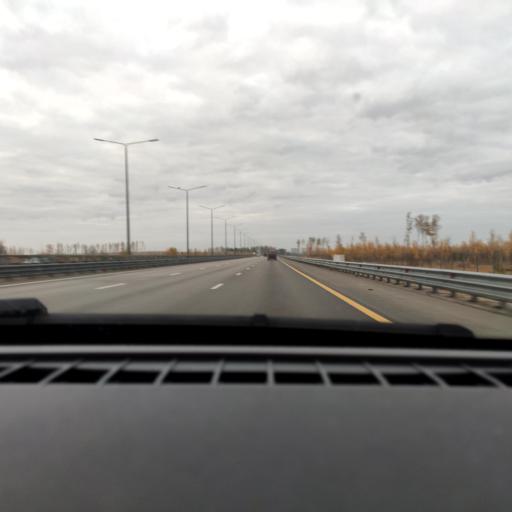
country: RU
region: Voronezj
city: Somovo
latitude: 51.7686
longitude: 39.3037
